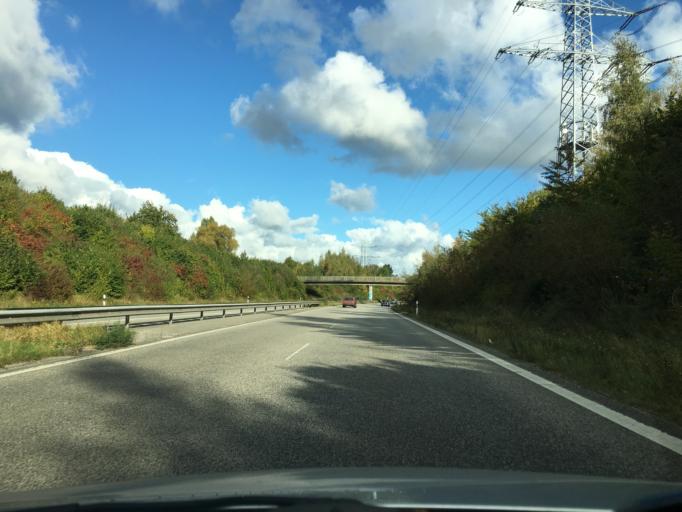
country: DE
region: Schleswig-Holstein
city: Monkeberg
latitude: 54.3354
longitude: 10.2053
